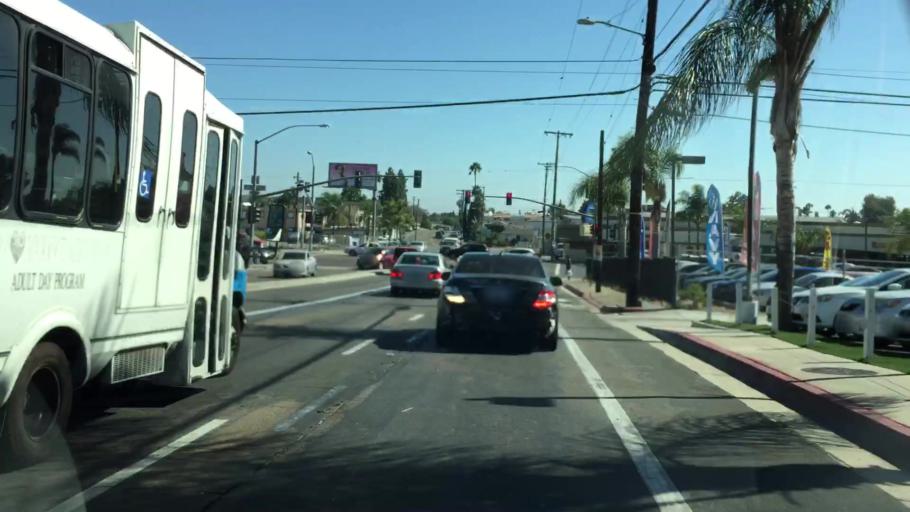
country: US
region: California
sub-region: San Diego County
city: La Mesa
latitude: 32.7694
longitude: -117.0472
